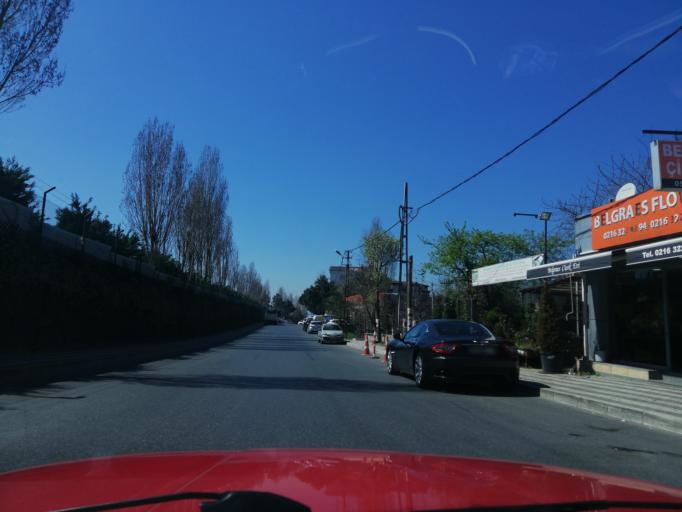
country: TR
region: Istanbul
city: Mahmut Sevket Pasa
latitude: 41.1183
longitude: 29.1213
